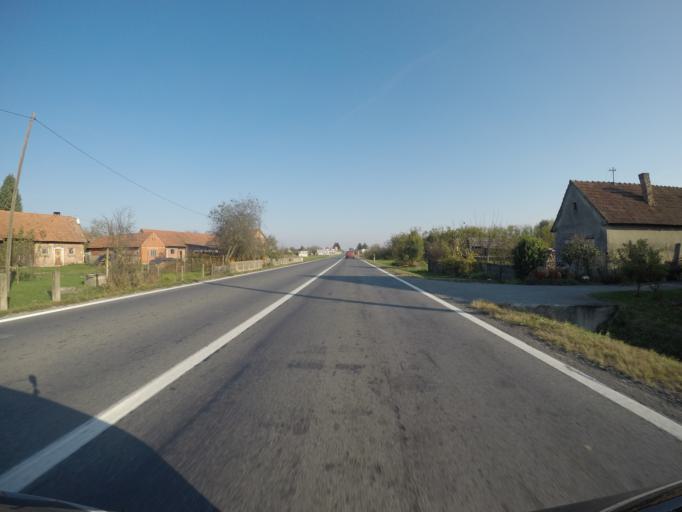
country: HR
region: Virovitick-Podravska
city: Pitomaca
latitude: 45.9684
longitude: 17.1968
